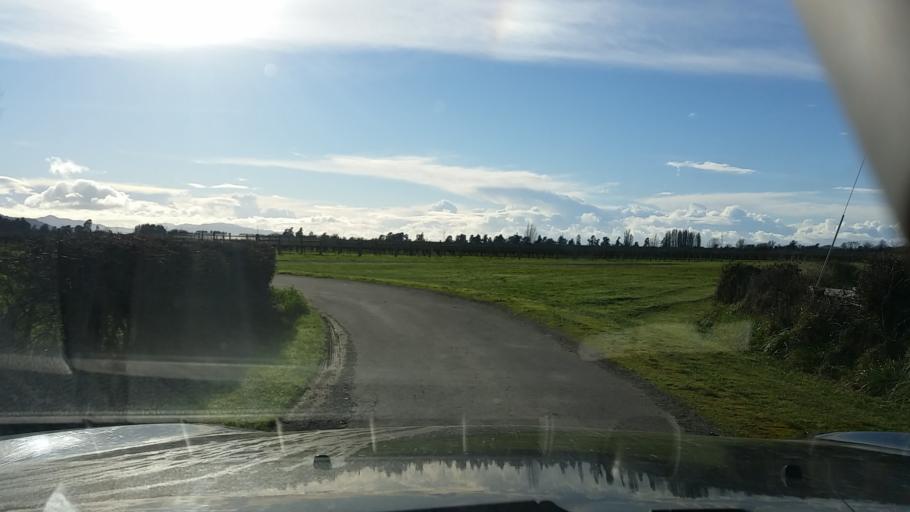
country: NZ
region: Marlborough
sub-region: Marlborough District
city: Blenheim
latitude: -41.4612
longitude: 173.9991
